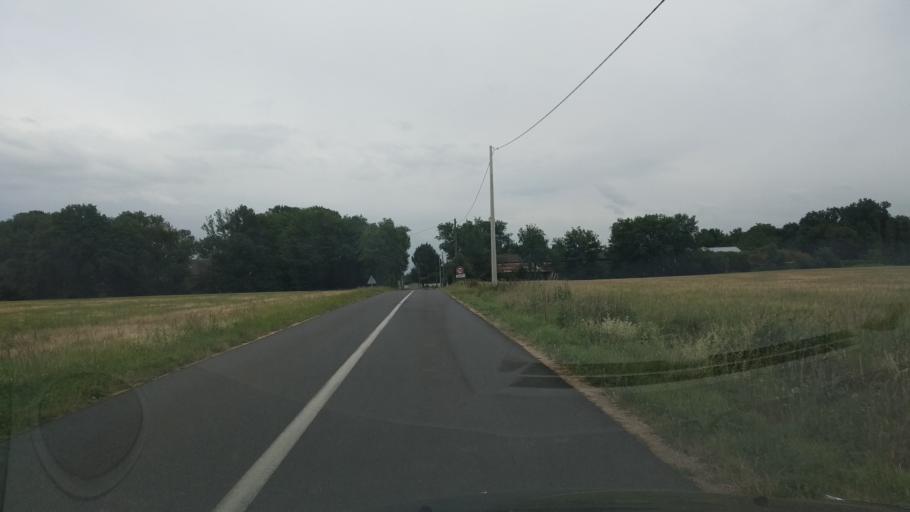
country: FR
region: Poitou-Charentes
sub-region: Departement de la Vienne
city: Vouneuil-sous-Biard
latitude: 46.5845
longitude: 0.2840
